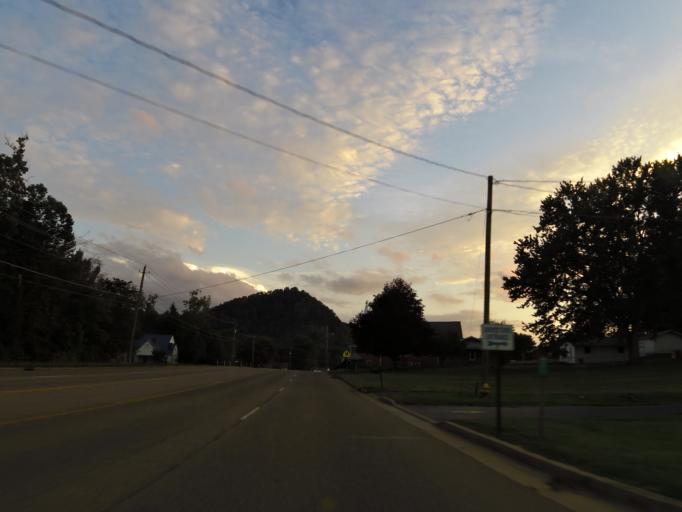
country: US
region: Tennessee
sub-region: Carter County
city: Hunter
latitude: 36.3859
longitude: -82.1413
